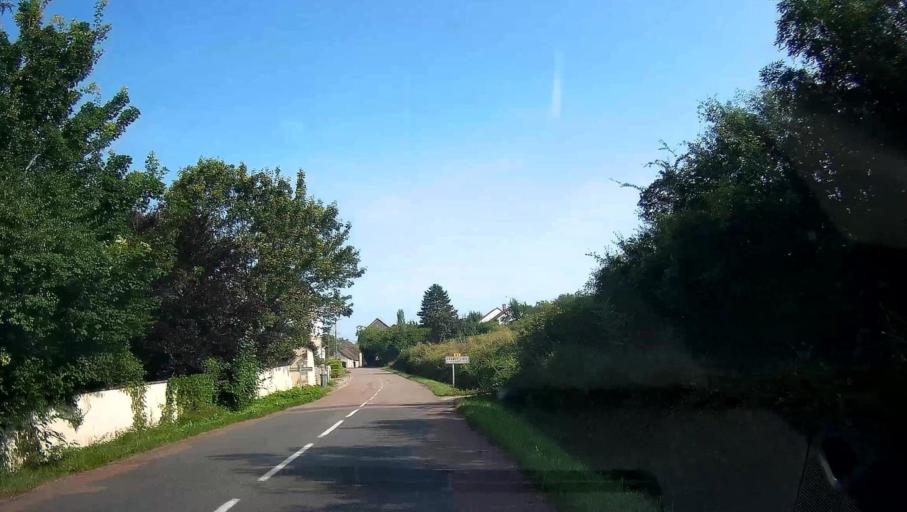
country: FR
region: Bourgogne
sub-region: Departement de Saone-et-Loire
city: Couches
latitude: 46.8893
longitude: 4.5988
